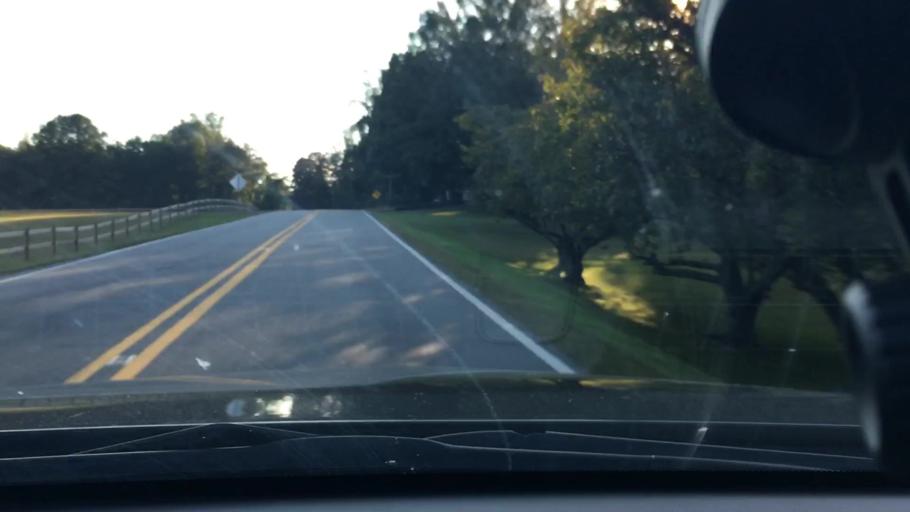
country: US
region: North Carolina
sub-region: Rutherford County
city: Rutherfordton
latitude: 35.3609
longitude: -81.9817
